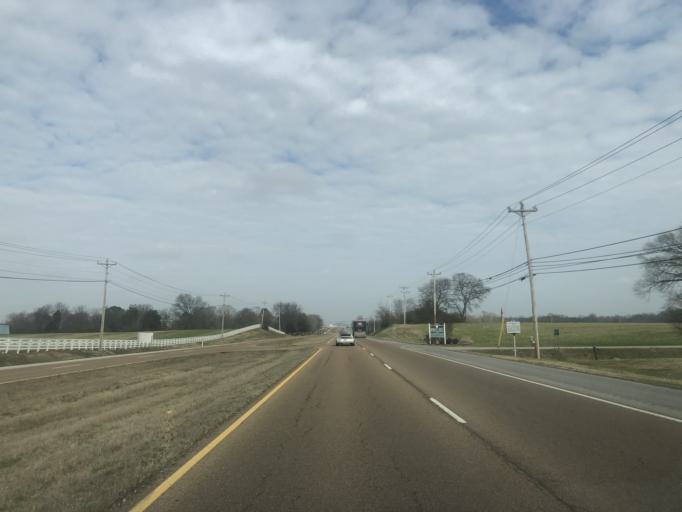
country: US
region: Tennessee
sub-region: Maury County
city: Spring Hill
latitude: 35.7223
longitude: -86.9654
